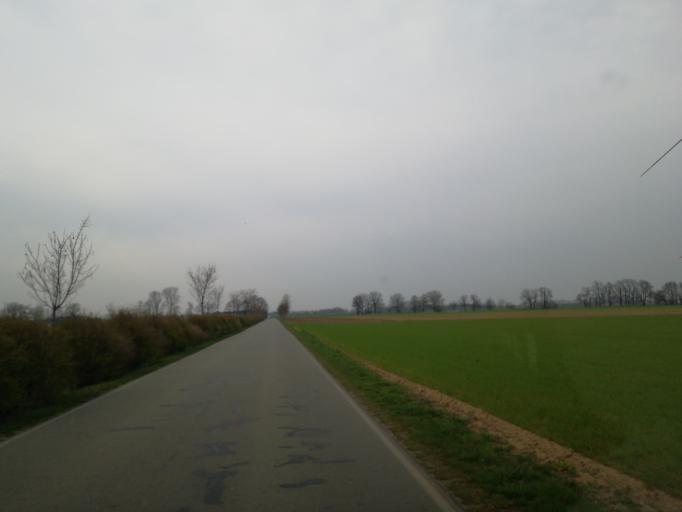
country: DE
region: Brandenburg
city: Elsterwerda
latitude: 51.4389
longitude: 13.4771
